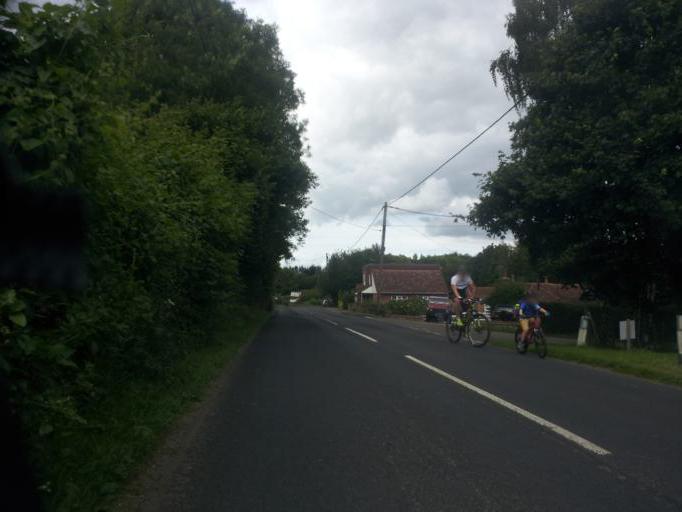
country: GB
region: England
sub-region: Kent
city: Wateringbury
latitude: 51.2674
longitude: 0.4295
